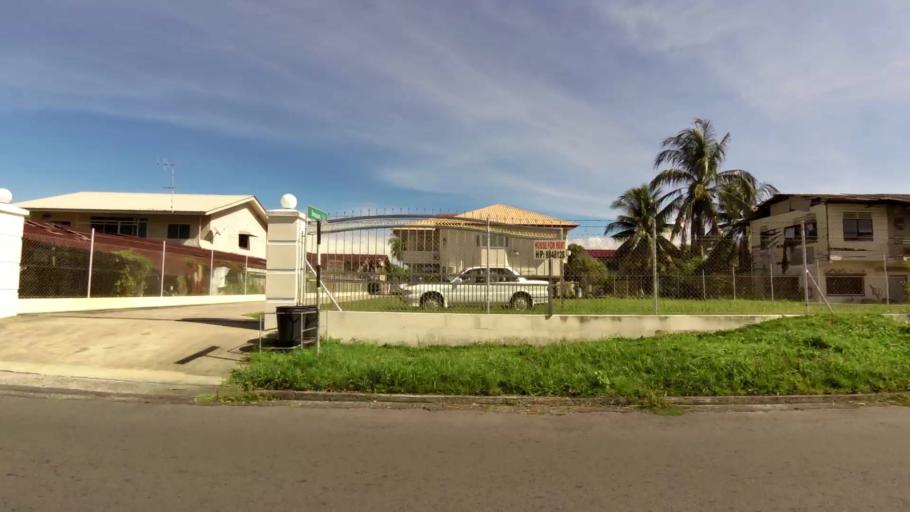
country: BN
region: Belait
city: Kuala Belait
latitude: 4.5862
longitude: 114.2083
